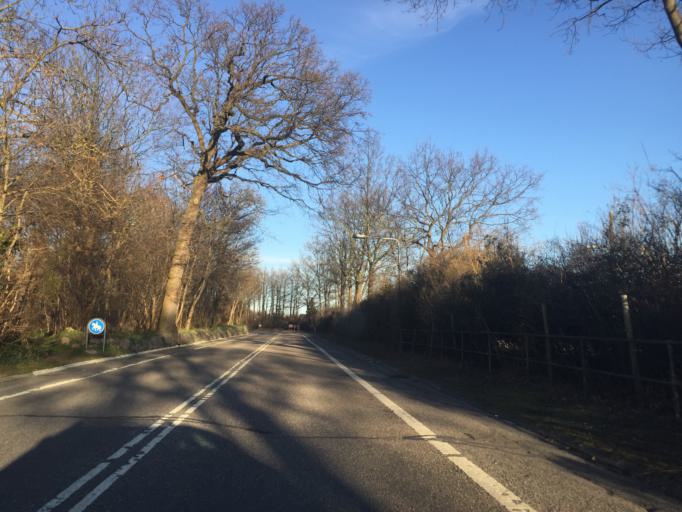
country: DK
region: Capital Region
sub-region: Dragor Kommune
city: Dragor
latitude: 55.5890
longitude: 12.6539
